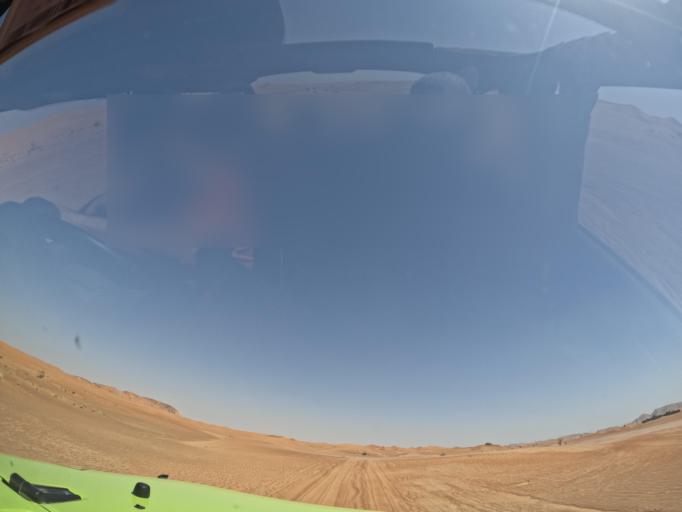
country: AE
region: Ash Shariqah
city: Adh Dhayd
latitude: 25.0035
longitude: 55.7326
